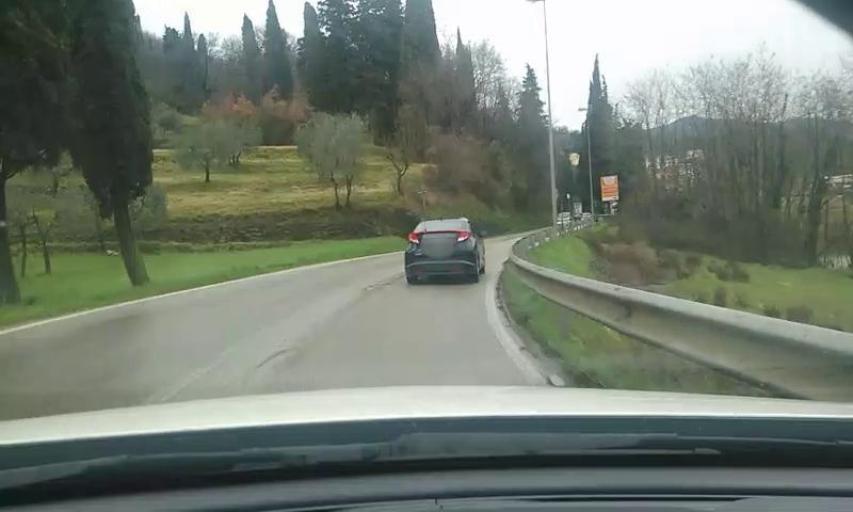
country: IT
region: Tuscany
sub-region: Provincia di Prato
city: Vaiano
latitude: 43.9426
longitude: 11.1257
